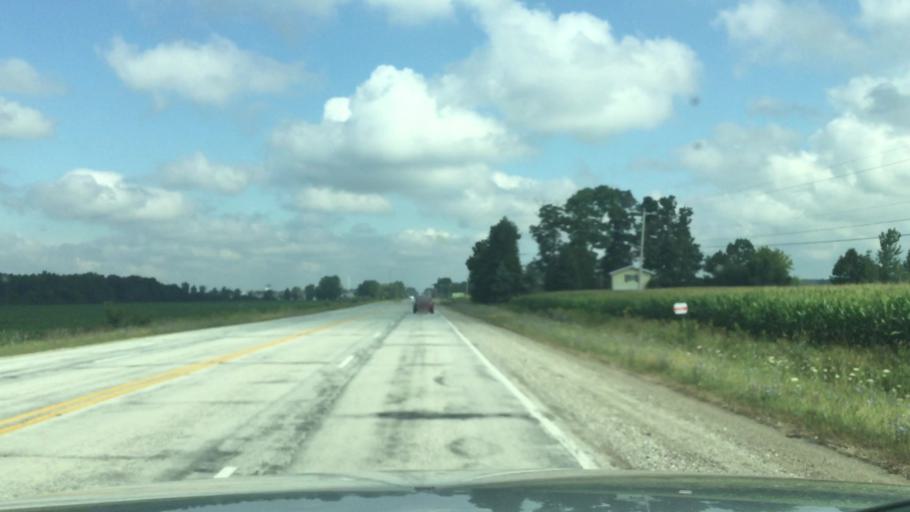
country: US
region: Michigan
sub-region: Saginaw County
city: Birch Run
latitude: 43.2361
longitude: -83.7586
